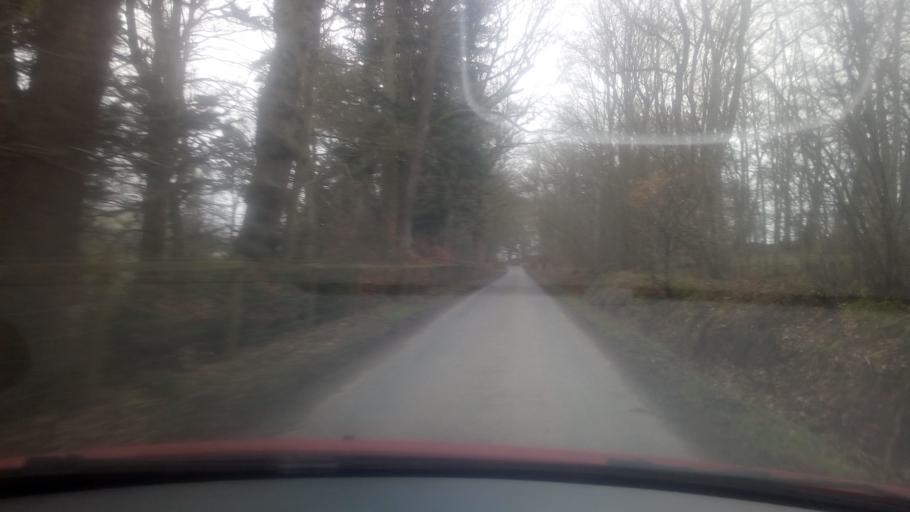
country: GB
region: Scotland
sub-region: The Scottish Borders
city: Jedburgh
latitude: 55.4176
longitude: -2.6456
